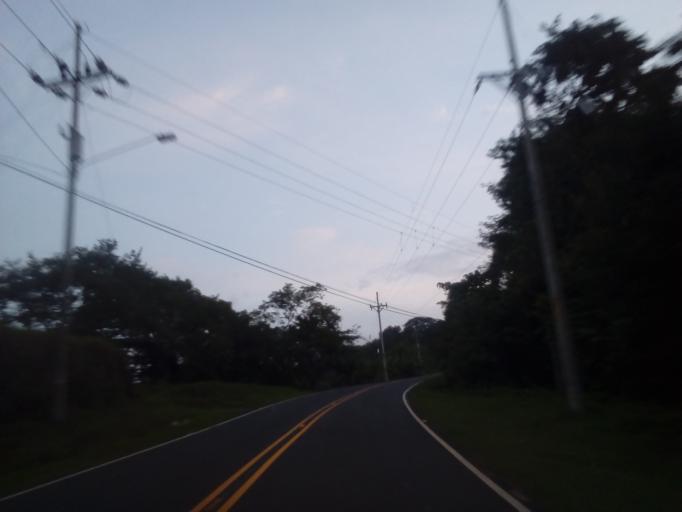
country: CR
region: Guanacaste
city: Hojancha
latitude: 10.0062
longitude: -85.5018
